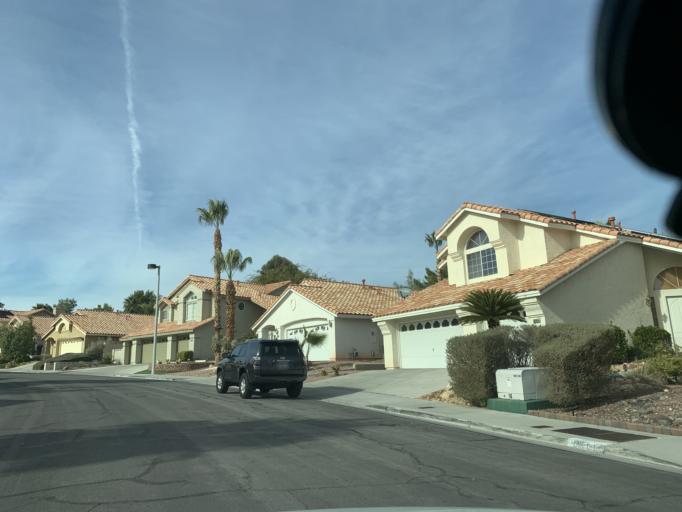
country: US
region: Nevada
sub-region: Clark County
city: Summerlin South
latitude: 36.1503
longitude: -115.3028
